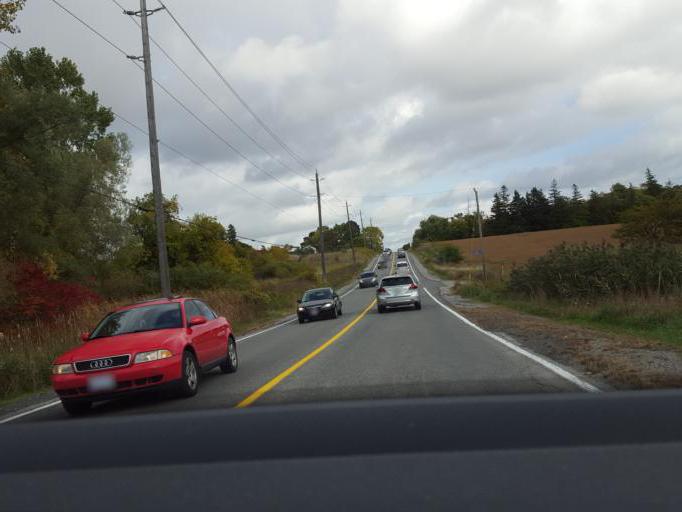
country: CA
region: Ontario
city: Pickering
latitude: 43.8505
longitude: -79.1908
